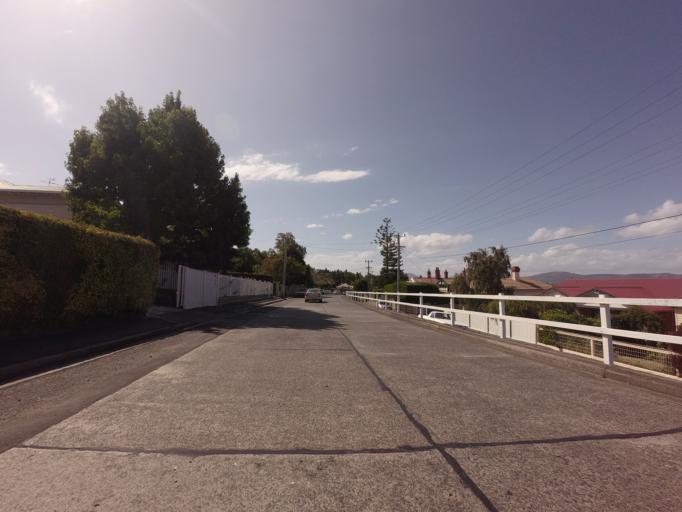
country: AU
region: Tasmania
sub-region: Hobart
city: Dynnyrne
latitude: -42.9004
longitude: 147.3169
